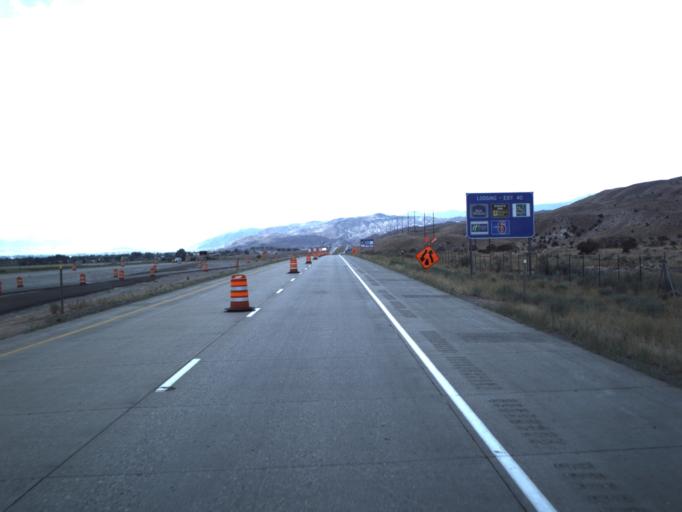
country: US
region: Utah
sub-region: Sevier County
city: Richfield
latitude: 38.8108
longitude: -112.0574
